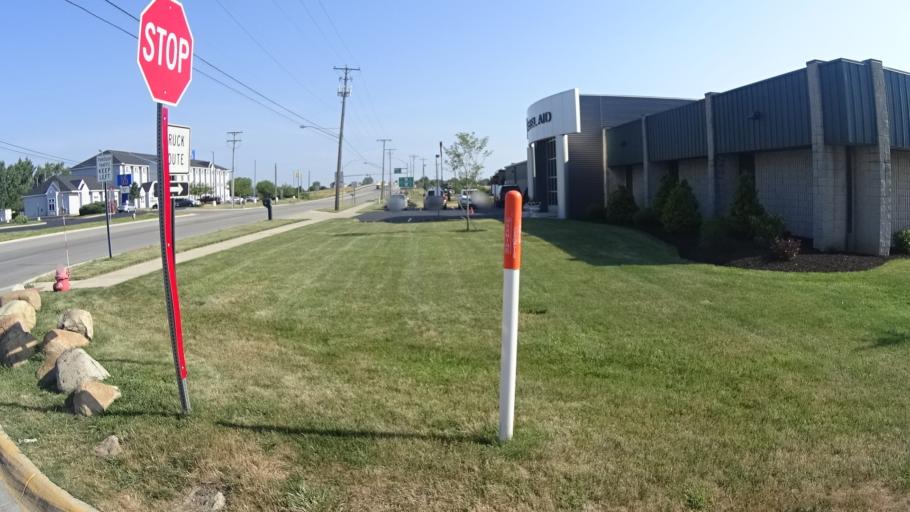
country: US
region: Ohio
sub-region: Erie County
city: Huron
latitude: 41.4013
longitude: -82.5910
